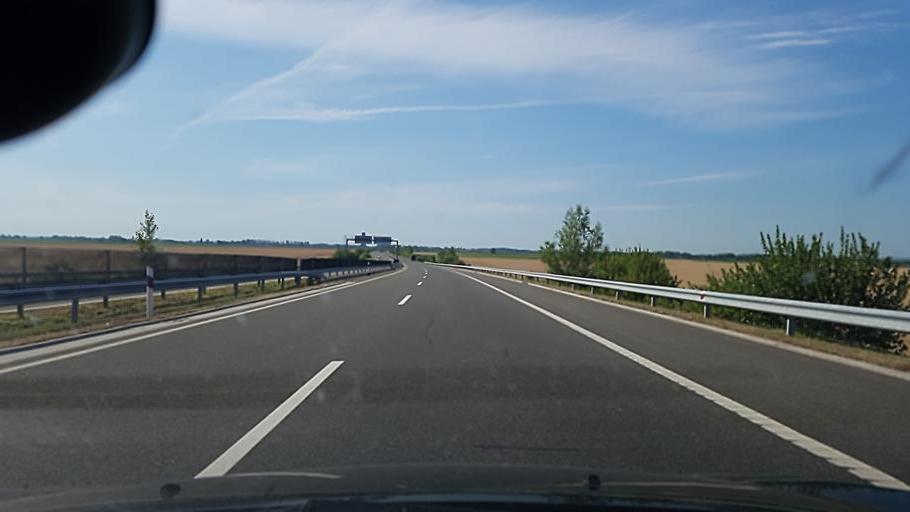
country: HU
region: Tolna
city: Szekszard
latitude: 46.3646
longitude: 18.7515
